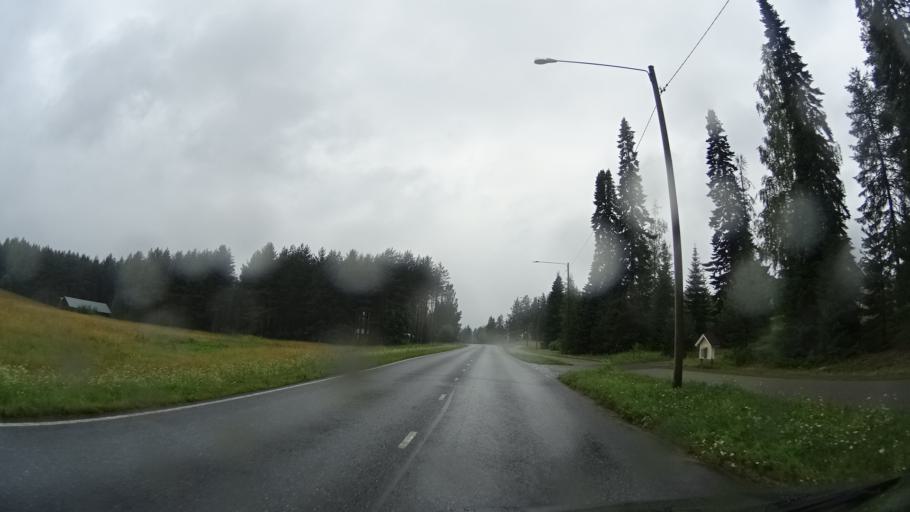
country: FI
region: North Karelia
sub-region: Keski-Karjala
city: Raeaekkylae
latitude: 62.3163
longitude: 29.6159
